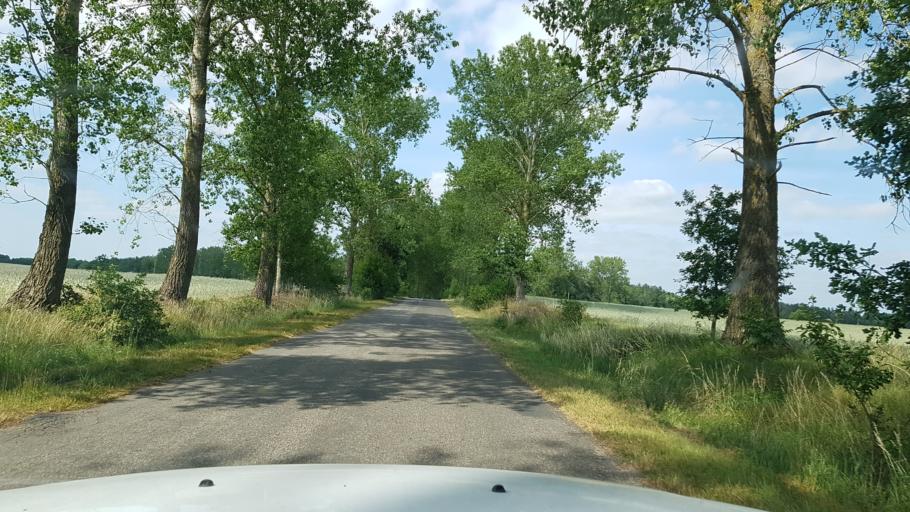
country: PL
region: West Pomeranian Voivodeship
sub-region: Powiat goleniowski
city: Mosty
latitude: 53.5790
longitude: 14.9814
